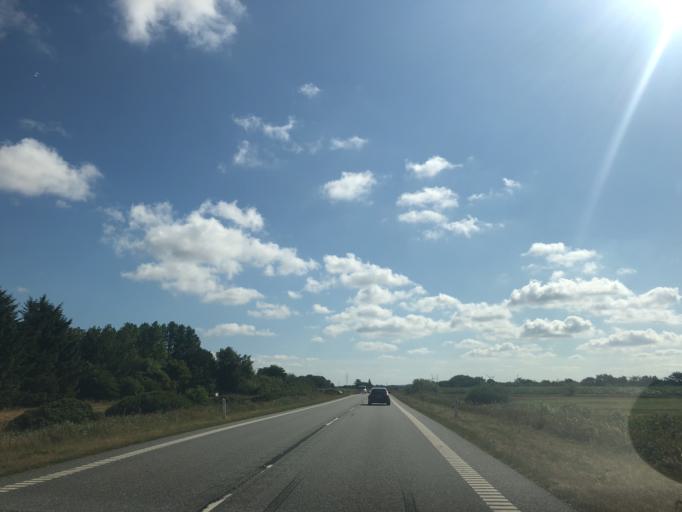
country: DK
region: North Denmark
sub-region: Jammerbugt Kommune
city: Fjerritslev
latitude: 57.0434
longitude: 9.1463
